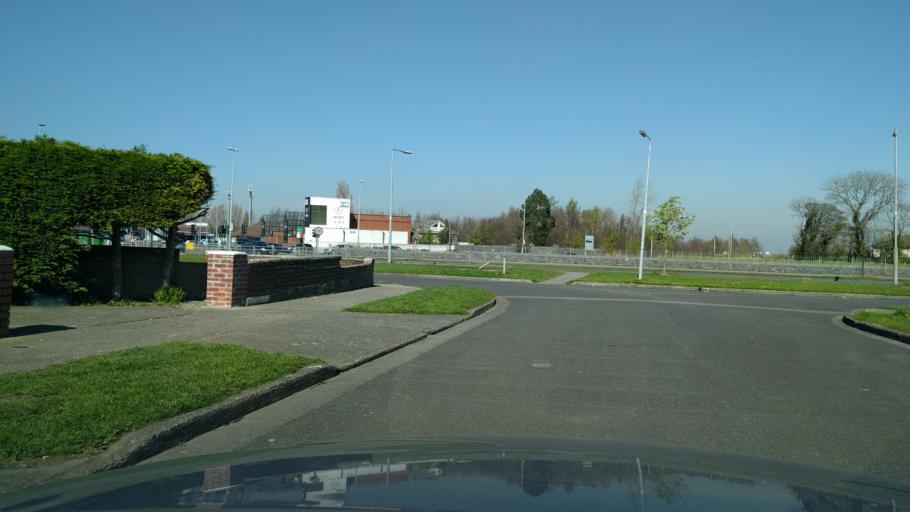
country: IE
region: Leinster
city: Firhouse
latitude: 53.2744
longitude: -6.3523
